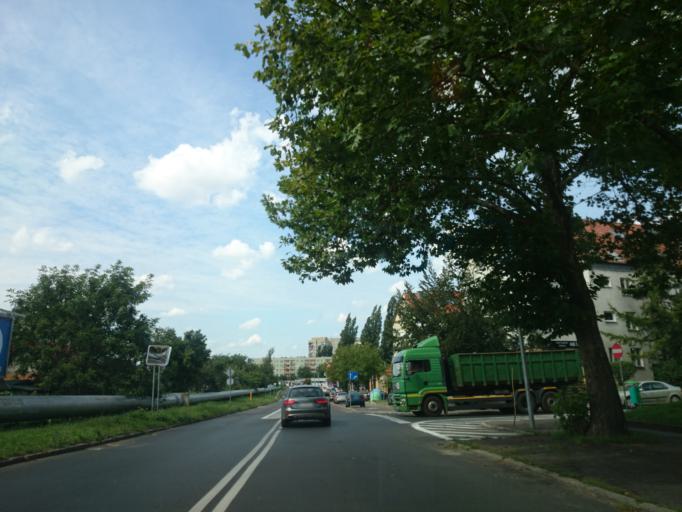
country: PL
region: West Pomeranian Voivodeship
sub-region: Szczecin
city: Szczecin
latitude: 53.4346
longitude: 14.4999
